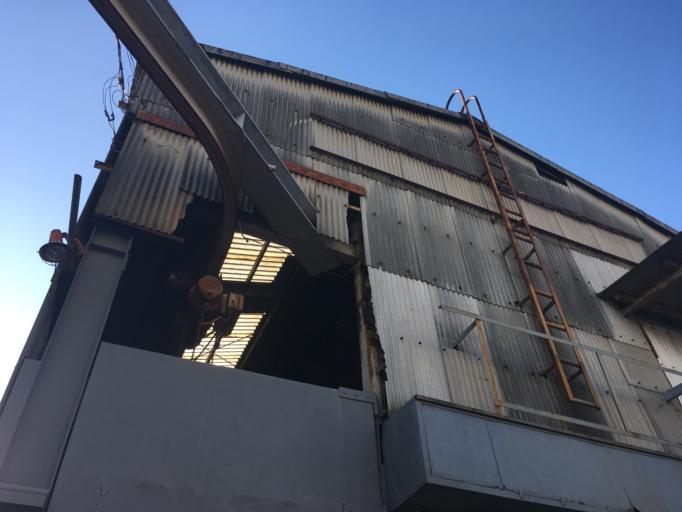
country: JP
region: Kanagawa
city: Minami-rinkan
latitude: 35.4603
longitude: 139.4702
